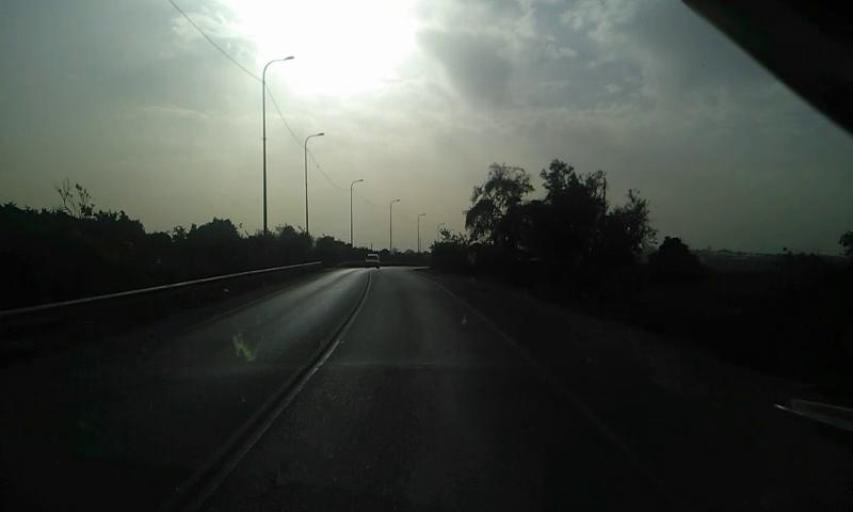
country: PS
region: West Bank
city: An Nabi Ilyas
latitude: 32.1867
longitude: 35.0057
